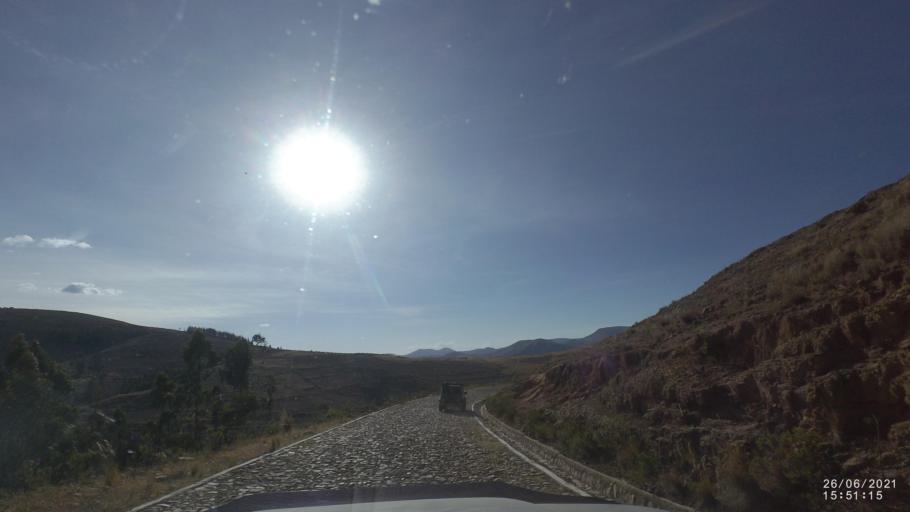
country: BO
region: Cochabamba
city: Arani
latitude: -17.8454
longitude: -65.7042
